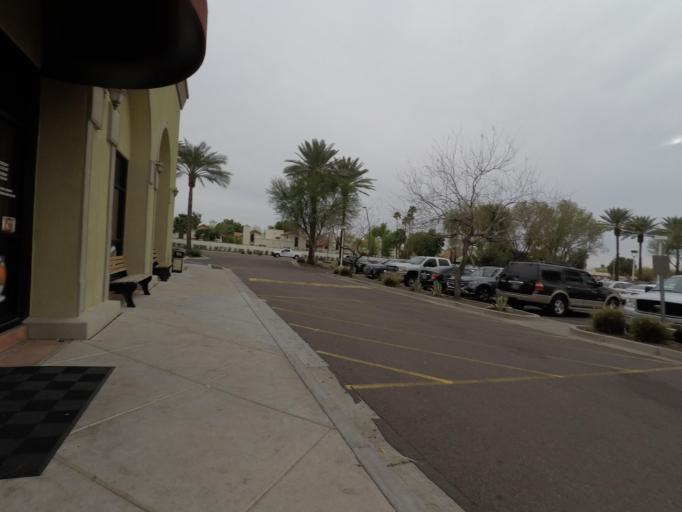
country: US
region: Arizona
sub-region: Maricopa County
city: San Carlos
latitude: 33.3352
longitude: -111.9072
